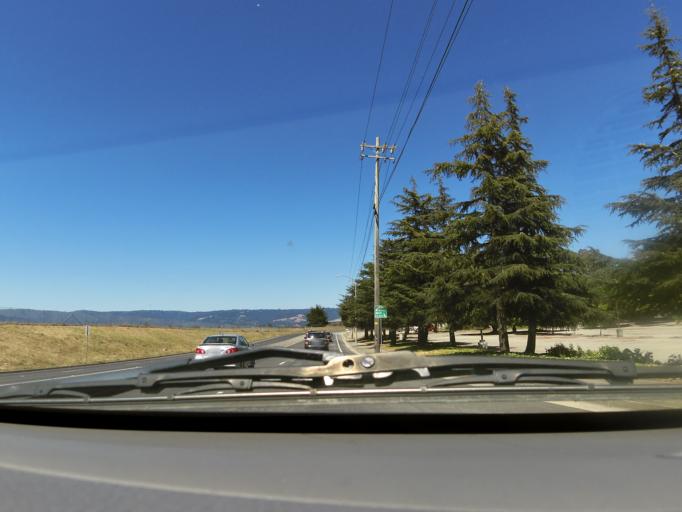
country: US
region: California
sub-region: Santa Cruz County
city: Freedom
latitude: 36.9287
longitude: -121.7942
